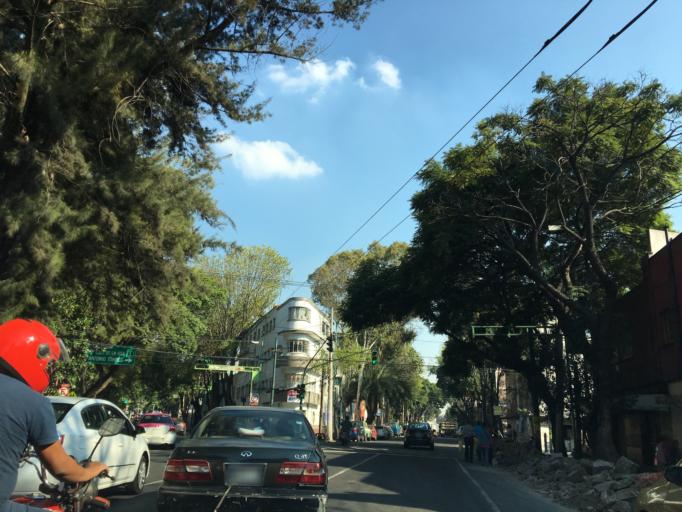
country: MX
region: Mexico City
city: Mexico City
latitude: 19.4121
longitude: -99.1332
